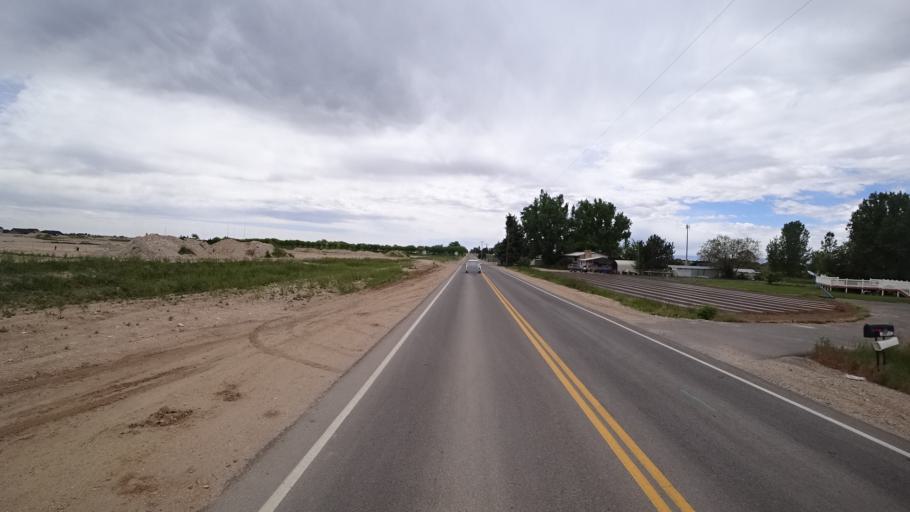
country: US
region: Idaho
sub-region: Ada County
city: Meridian
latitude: 43.5744
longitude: -116.4138
